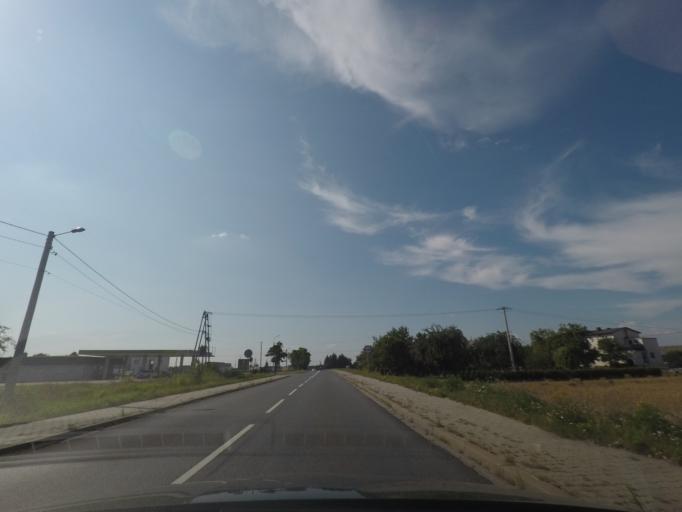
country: PL
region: Silesian Voivodeship
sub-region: Powiat pszczynski
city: Radostowice
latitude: 50.0069
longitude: 18.8692
